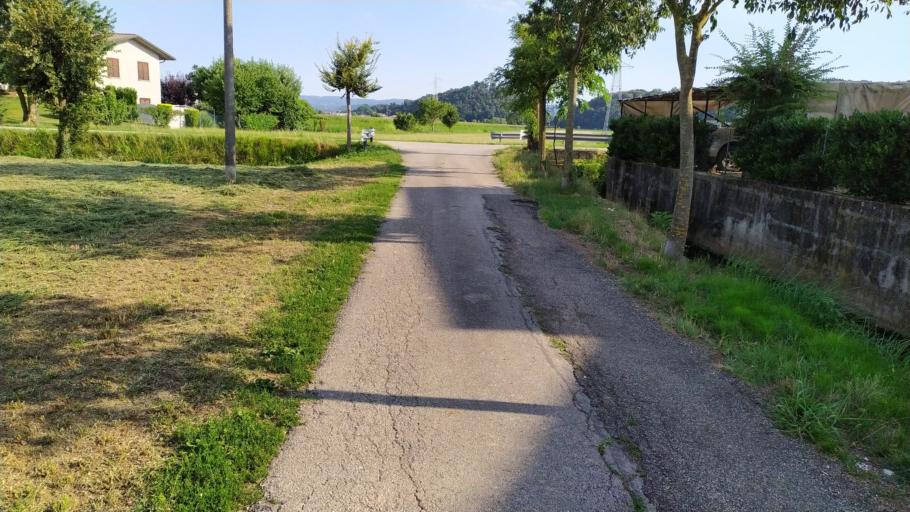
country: IT
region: Veneto
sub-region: Provincia di Vicenza
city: Costabissara
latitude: 45.5643
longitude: 11.4871
